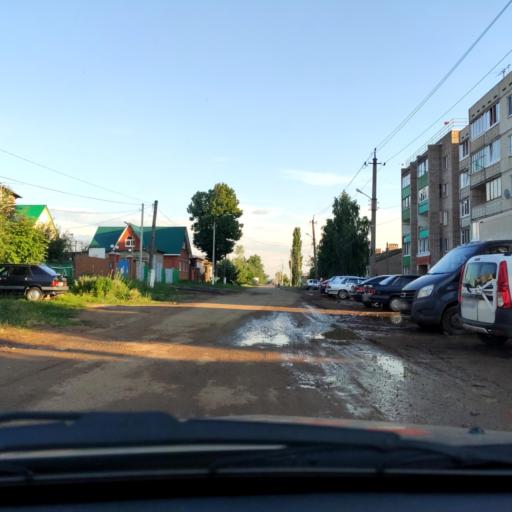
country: RU
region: Bashkortostan
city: Blagoveshchensk
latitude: 55.0302
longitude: 55.9774
